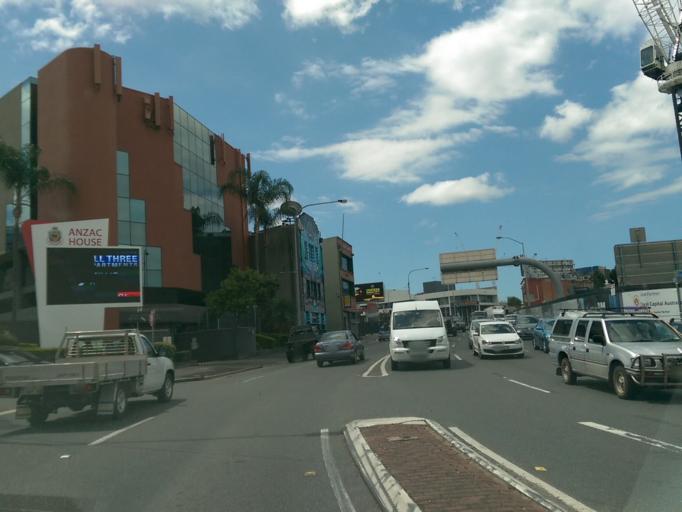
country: AU
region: Queensland
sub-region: Brisbane
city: Fortitude Valley
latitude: -27.4575
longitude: 153.0313
